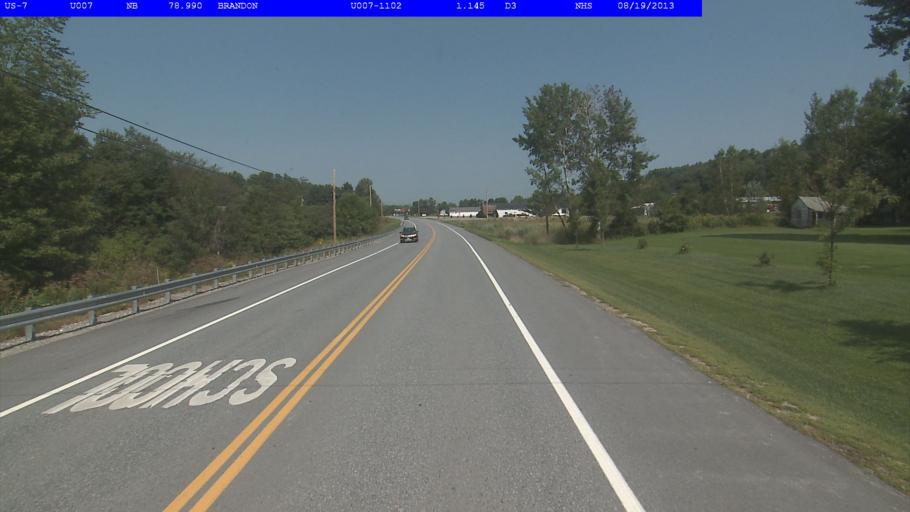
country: US
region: Vermont
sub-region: Rutland County
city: Brandon
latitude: 43.7707
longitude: -73.0514
